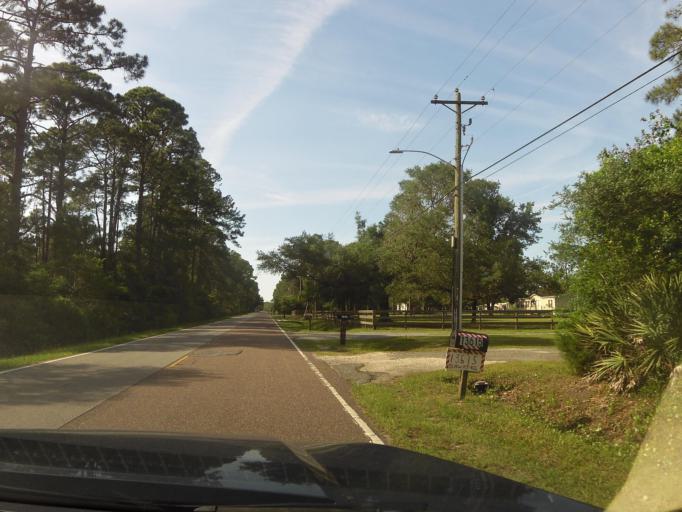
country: US
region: Florida
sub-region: Duval County
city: Atlantic Beach
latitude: 30.4829
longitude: -81.4713
